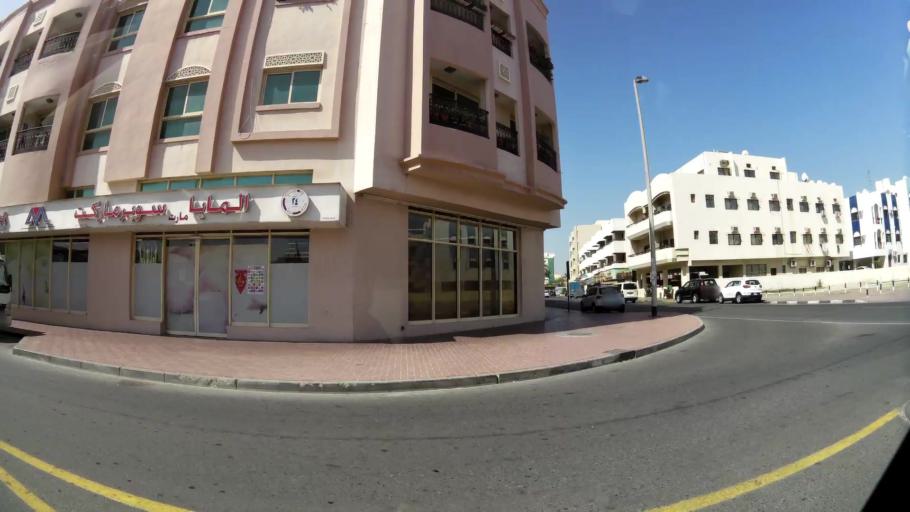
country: AE
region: Ash Shariqah
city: Sharjah
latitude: 25.2379
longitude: 55.2777
